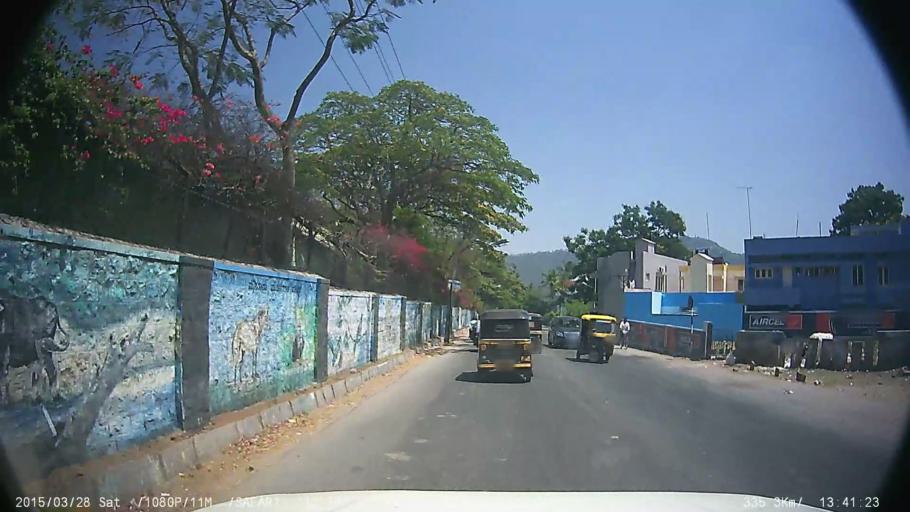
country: IN
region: Karnataka
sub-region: Mysore
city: Mysore
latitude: 12.3015
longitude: 76.6643
